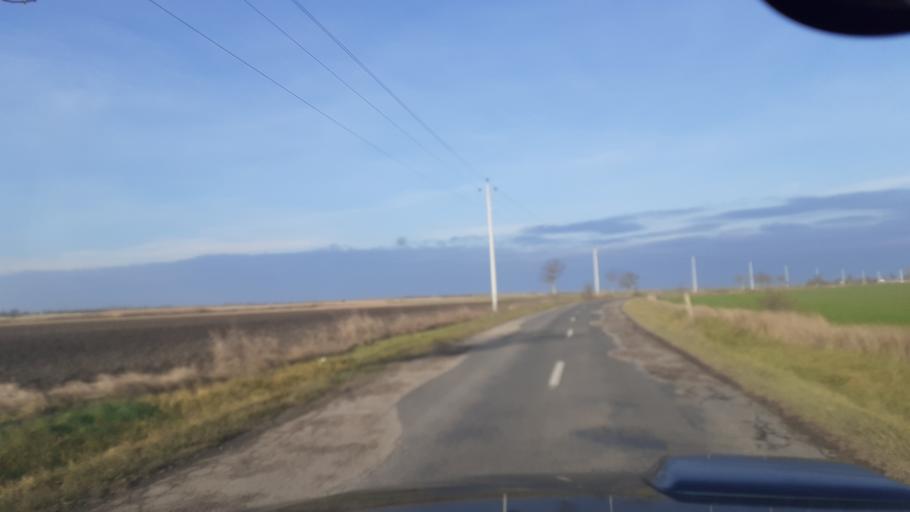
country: HU
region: Pest
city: Domsod
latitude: 47.1002
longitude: 19.0473
